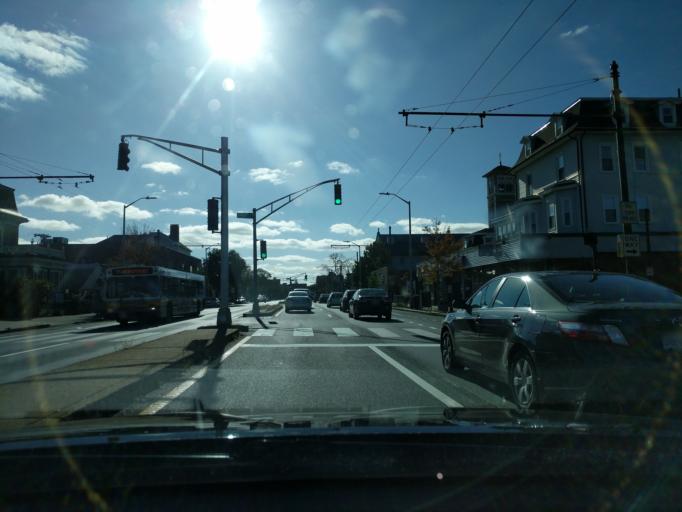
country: US
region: Massachusetts
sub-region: Middlesex County
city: Somerville
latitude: 42.3955
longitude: -71.1281
